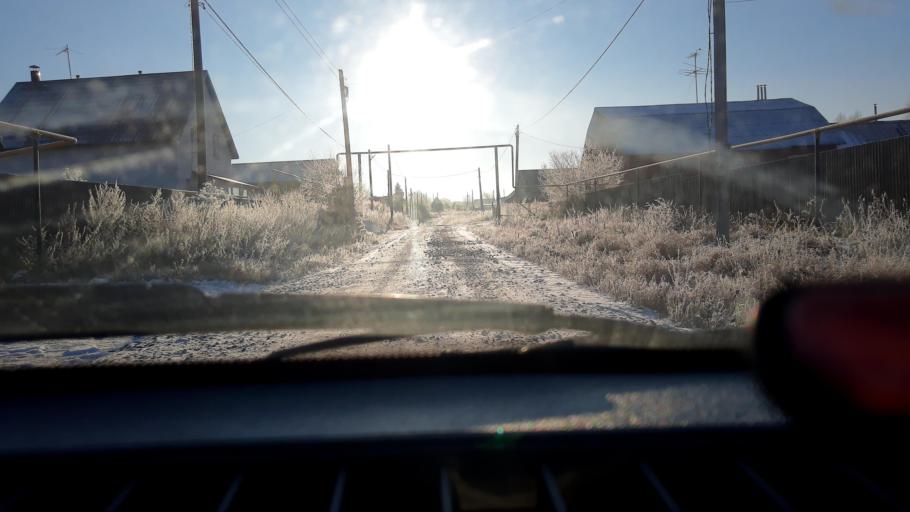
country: RU
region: Bashkortostan
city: Mikhaylovka
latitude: 54.8702
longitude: 55.7596
